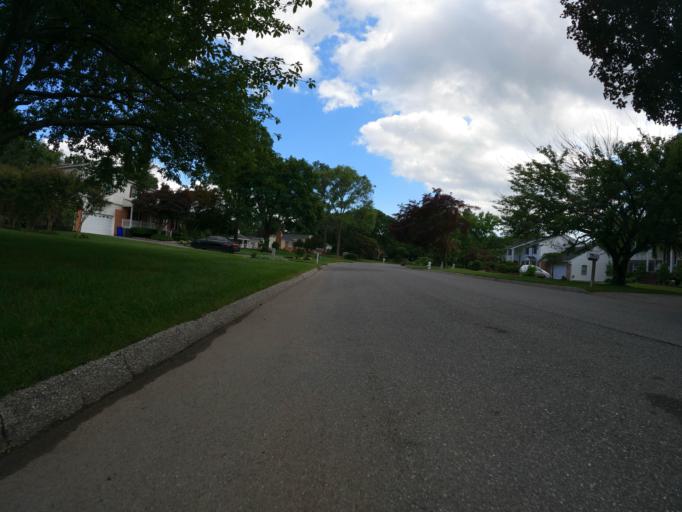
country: US
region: Maryland
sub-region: Howard County
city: Columbia
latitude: 39.2290
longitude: -76.8660
